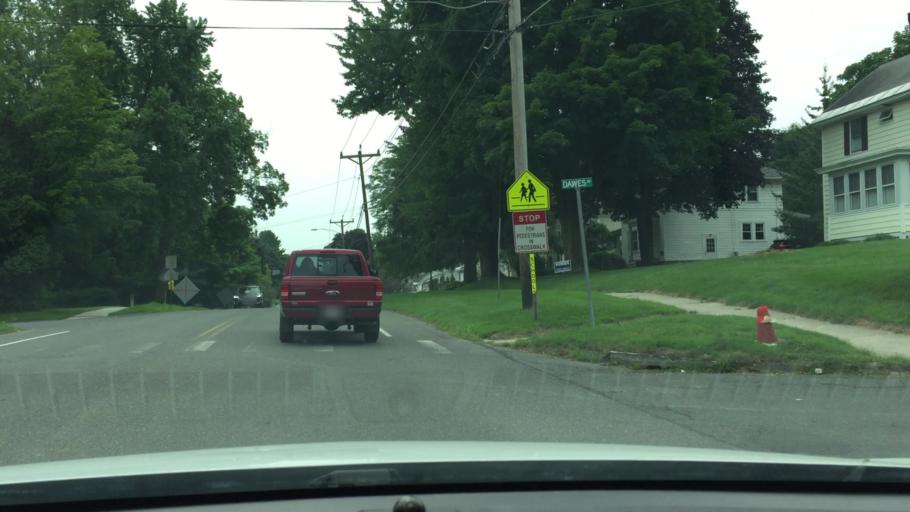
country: US
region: Massachusetts
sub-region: Berkshire County
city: Pittsfield
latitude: 42.4388
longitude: -73.2360
